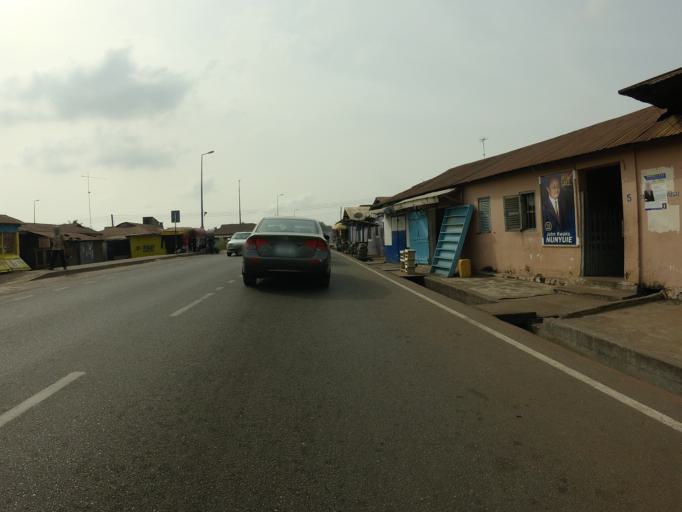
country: GH
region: Volta
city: Ho
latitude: 6.6081
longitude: 0.4749
